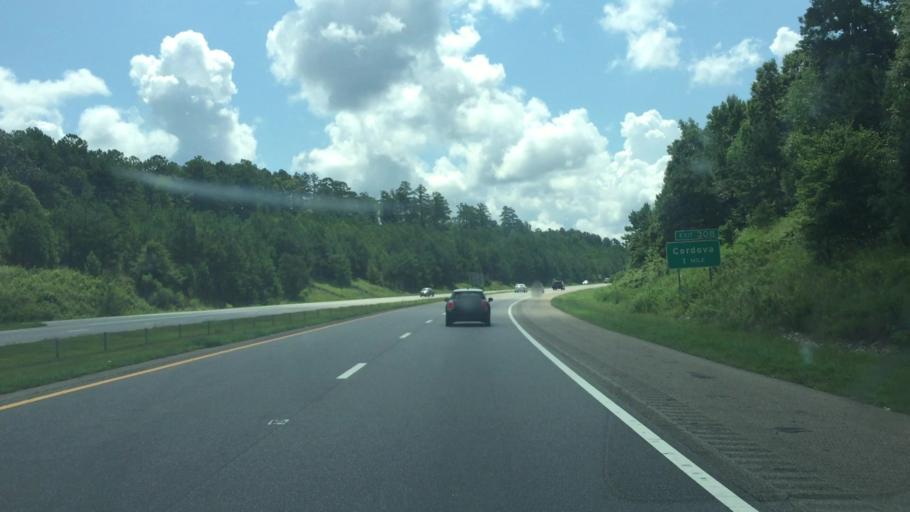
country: US
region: North Carolina
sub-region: Richmond County
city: Cordova
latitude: 34.9455
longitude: -79.8473
